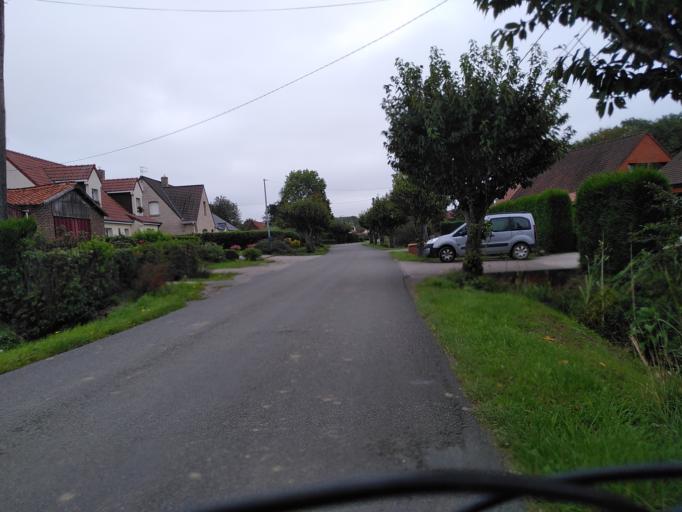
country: FR
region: Nord-Pas-de-Calais
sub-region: Departement du Pas-de-Calais
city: Saint-Venant
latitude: 50.6262
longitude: 2.5291
